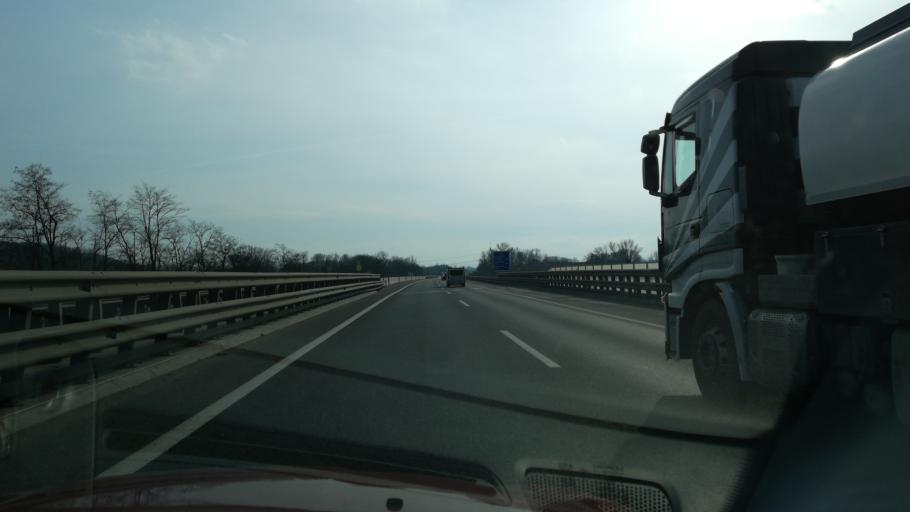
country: AT
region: Lower Austria
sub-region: Politischer Bezirk Sankt Polten
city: Traismauer
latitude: 48.3372
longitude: 15.7232
